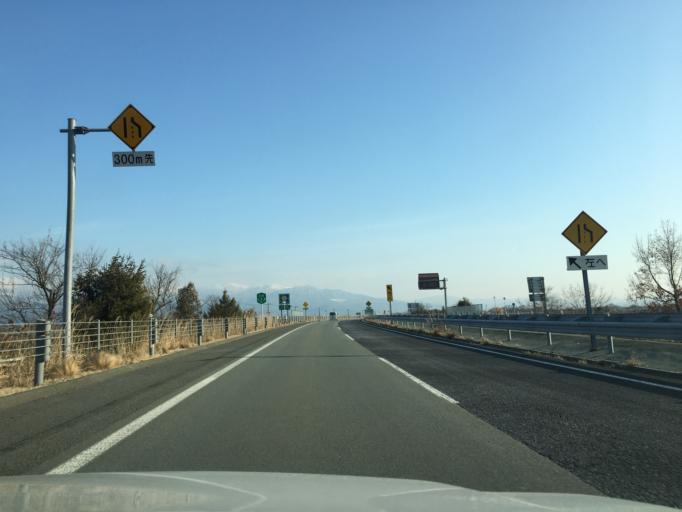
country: JP
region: Yamagata
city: Sagae
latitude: 38.3549
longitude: 140.2953
